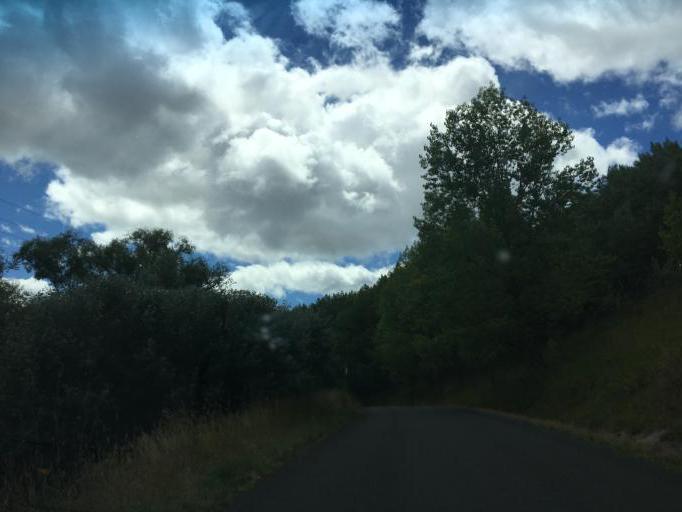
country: NZ
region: Hawke's Bay
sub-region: Hastings District
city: Hastings
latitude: -39.7484
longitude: 176.8868
